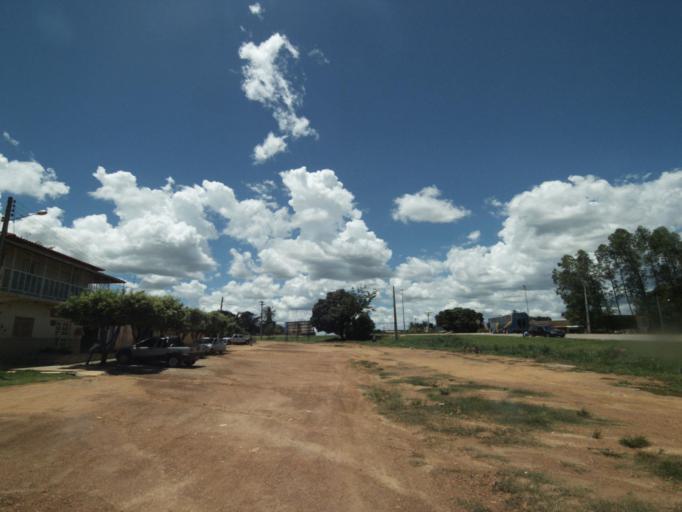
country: BR
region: Goias
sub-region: Barro Alto
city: Barro Alto
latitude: -15.2097
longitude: -48.6999
